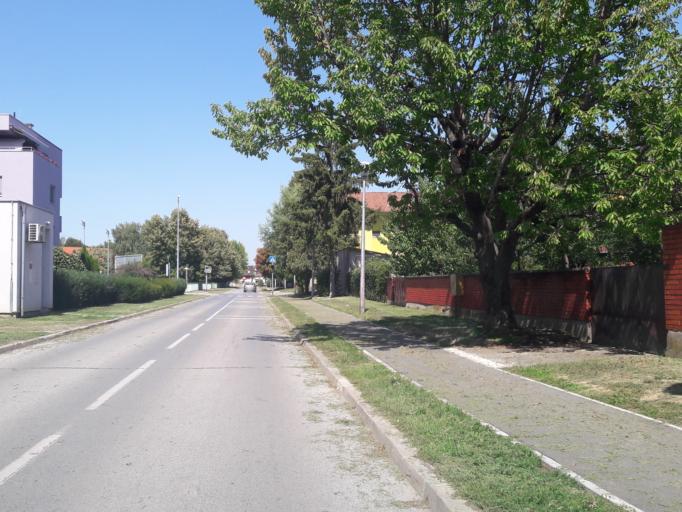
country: HR
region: Osjecko-Baranjska
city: Visnjevac
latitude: 45.5606
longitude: 18.6423
